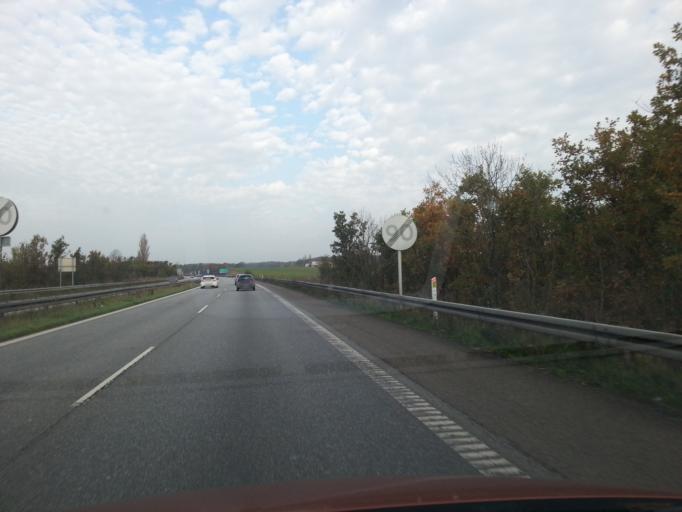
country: DK
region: Zealand
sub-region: Vordingborg Kommune
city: Nyrad
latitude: 54.9723
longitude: 12.0039
